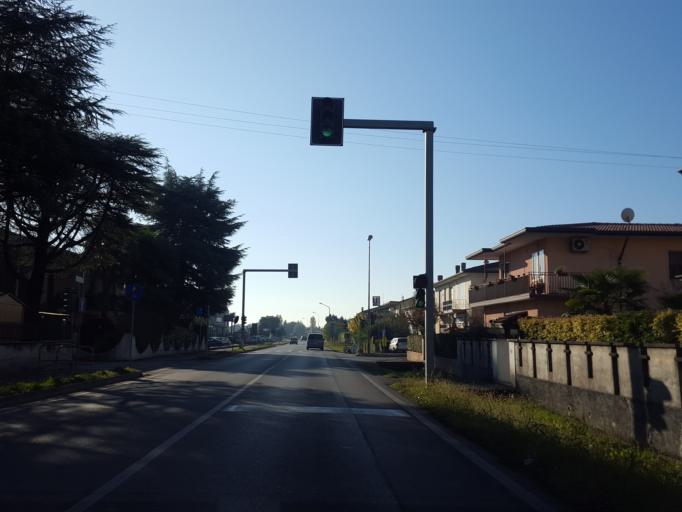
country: IT
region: Veneto
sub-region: Provincia di Vicenza
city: Marola
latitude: 45.5328
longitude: 11.6304
